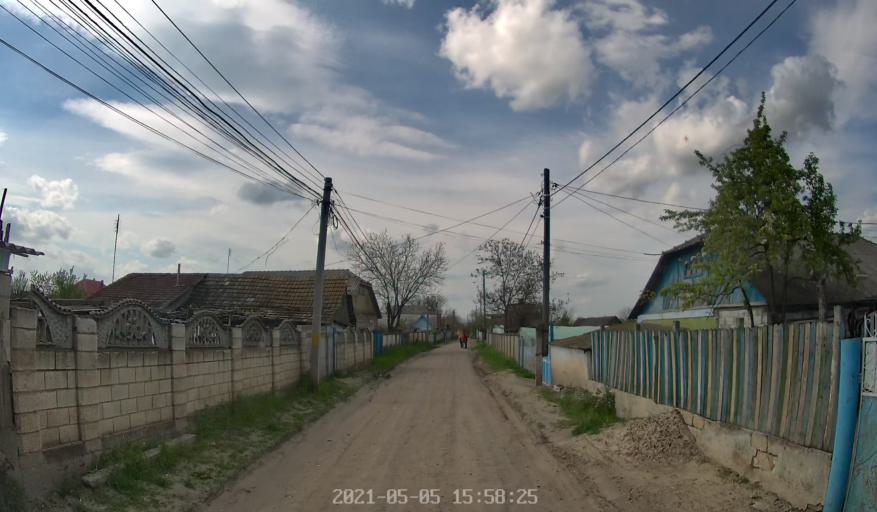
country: MD
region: Criuleni
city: Criuleni
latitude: 47.1381
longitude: 29.2039
